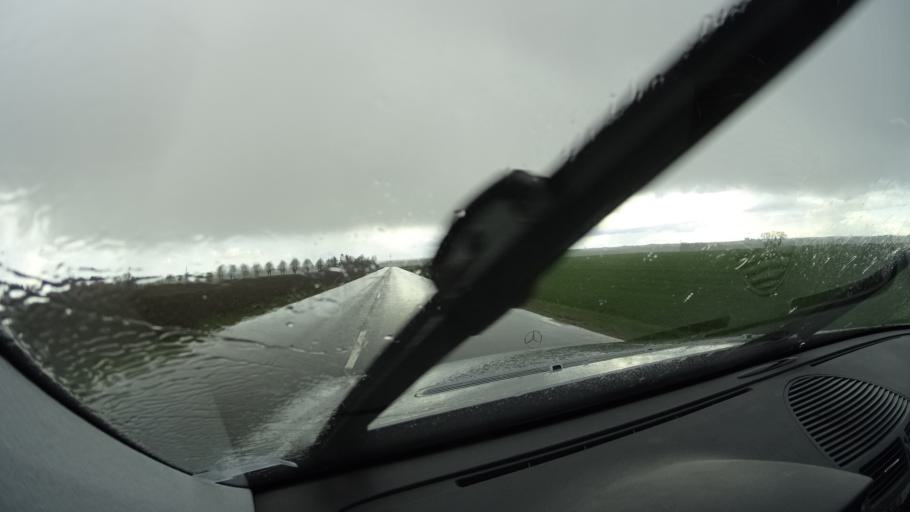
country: SE
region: Skane
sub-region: Lunds Kommun
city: Lund
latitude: 55.7628
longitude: 13.2232
